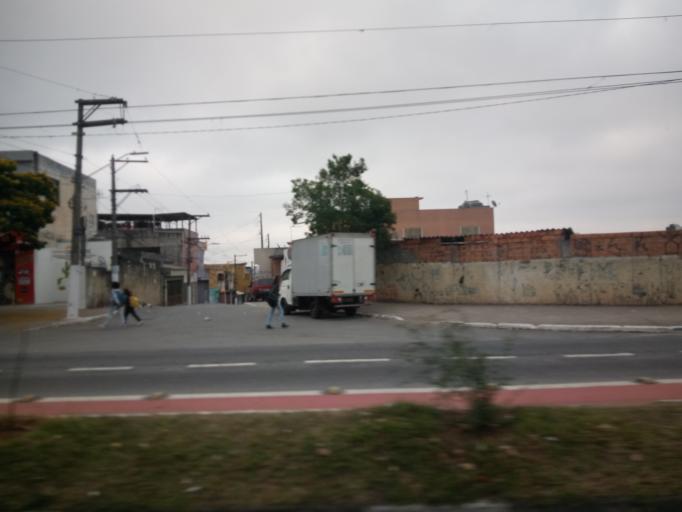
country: BR
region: Sao Paulo
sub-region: Diadema
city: Diadema
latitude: -23.6674
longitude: -46.6363
